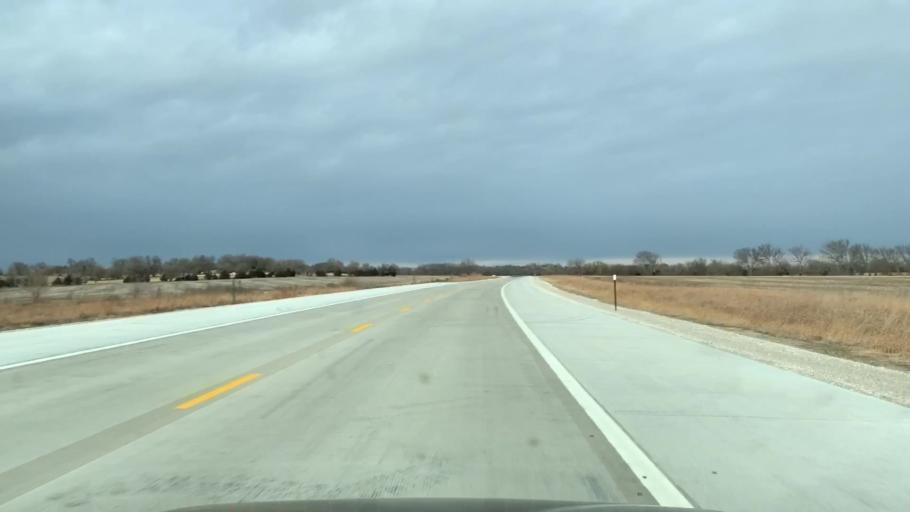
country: US
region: Kansas
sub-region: Allen County
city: Humboldt
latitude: 37.8560
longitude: -95.4082
